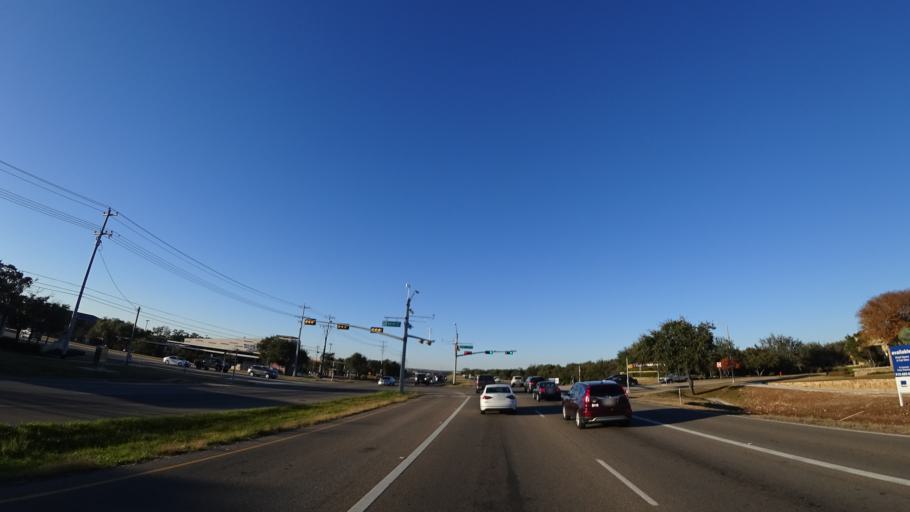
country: US
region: Texas
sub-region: Williamson County
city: Brushy Creek
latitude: 30.5226
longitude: -97.7743
